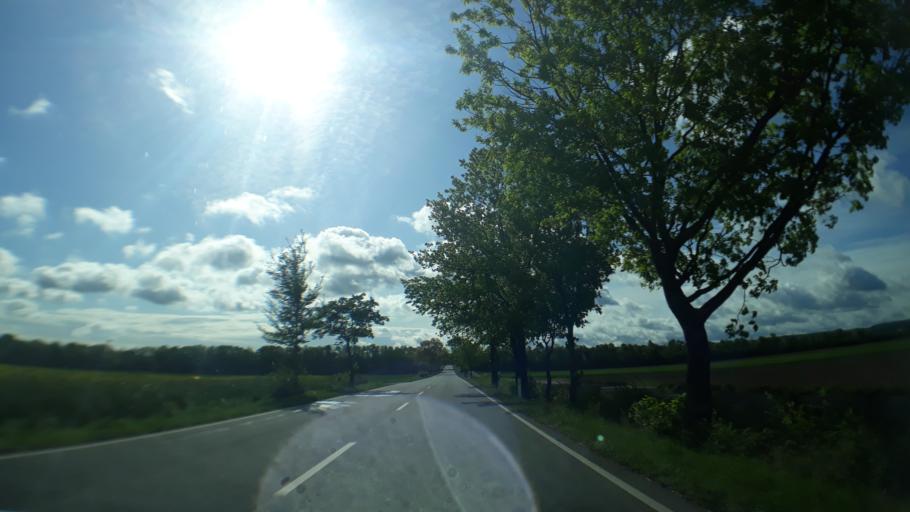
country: DE
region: North Rhine-Westphalia
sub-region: Regierungsbezirk Koln
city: Euskirchen
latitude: 50.6685
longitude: 6.7232
